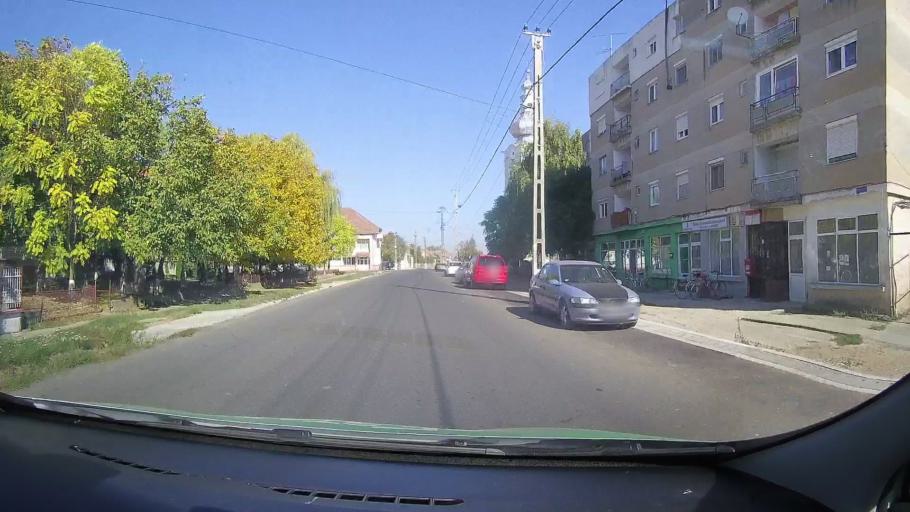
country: RO
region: Satu Mare
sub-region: Comuna Berveni
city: Berveni
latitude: 47.7547
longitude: 22.4722
